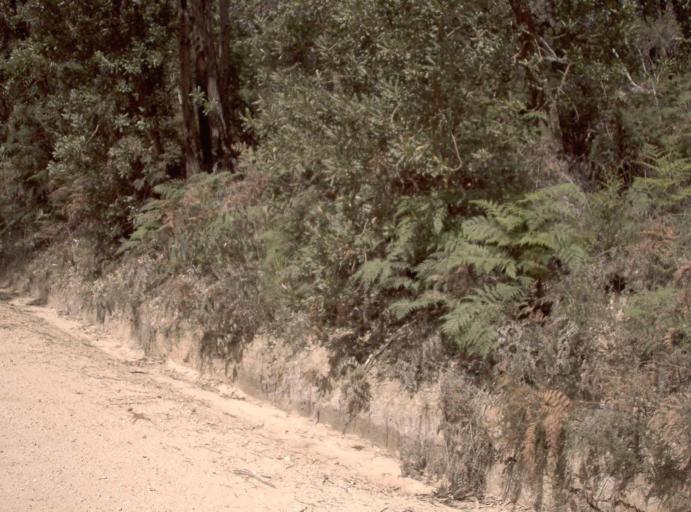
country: AU
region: Victoria
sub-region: East Gippsland
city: Lakes Entrance
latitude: -37.6575
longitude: 148.6394
